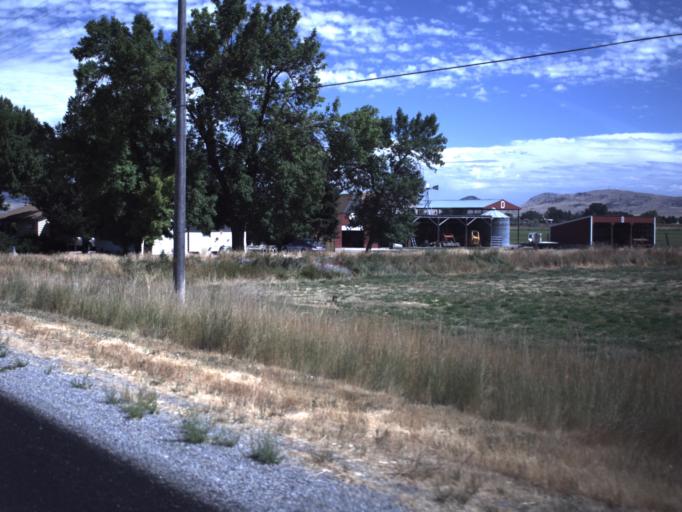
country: US
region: Utah
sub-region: Box Elder County
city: Garland
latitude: 41.7627
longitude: -112.1486
